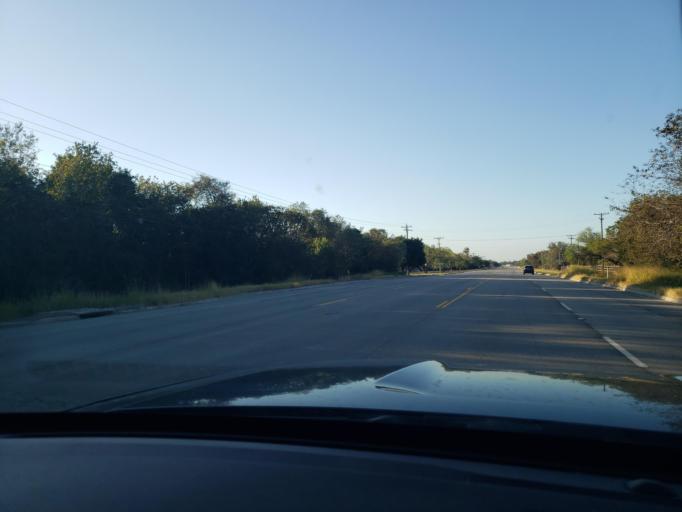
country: US
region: Texas
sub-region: Bee County
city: Beeville
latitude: 28.4324
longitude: -97.7144
